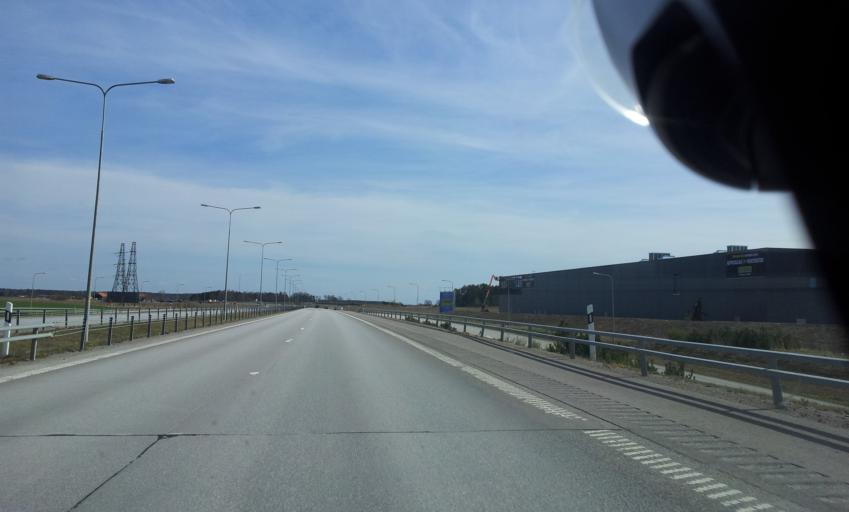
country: SE
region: Uppsala
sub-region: Uppsala Kommun
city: Gamla Uppsala
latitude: 59.8879
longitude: 17.6698
